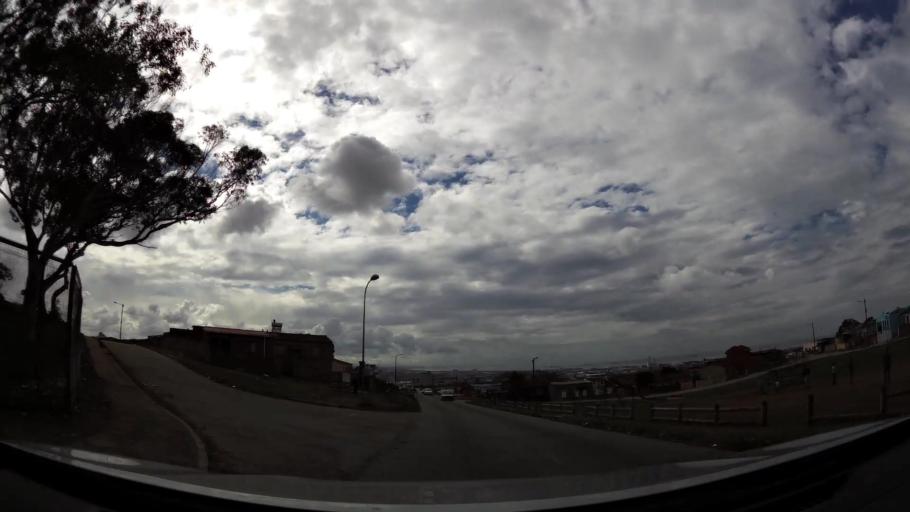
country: ZA
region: Eastern Cape
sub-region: Nelson Mandela Bay Metropolitan Municipality
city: Port Elizabeth
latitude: -33.9331
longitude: 25.5657
